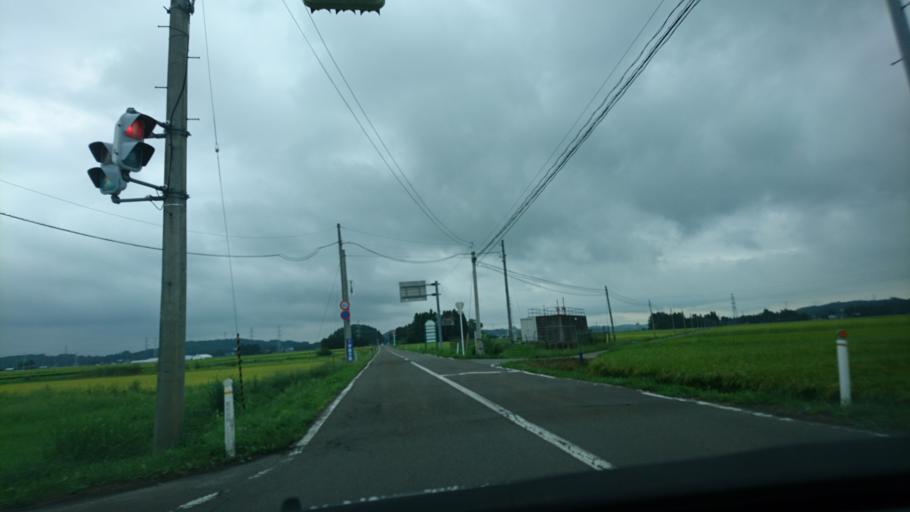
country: JP
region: Iwate
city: Ichinoseki
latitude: 38.8093
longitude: 140.9515
